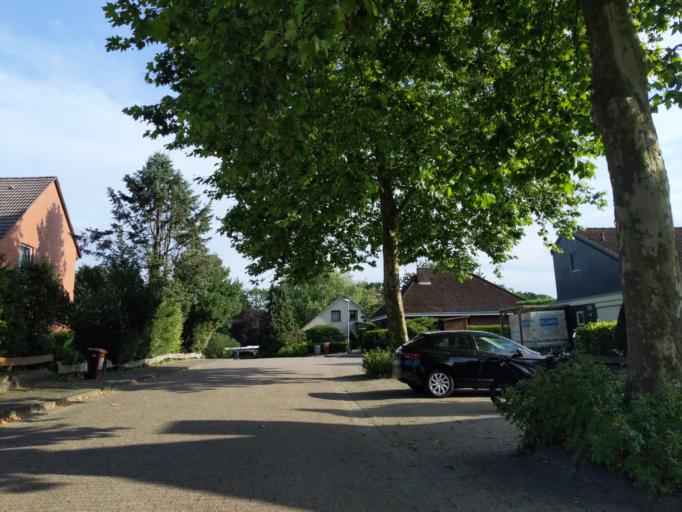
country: DE
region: Lower Saxony
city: Stade
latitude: 53.5818
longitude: 9.4611
